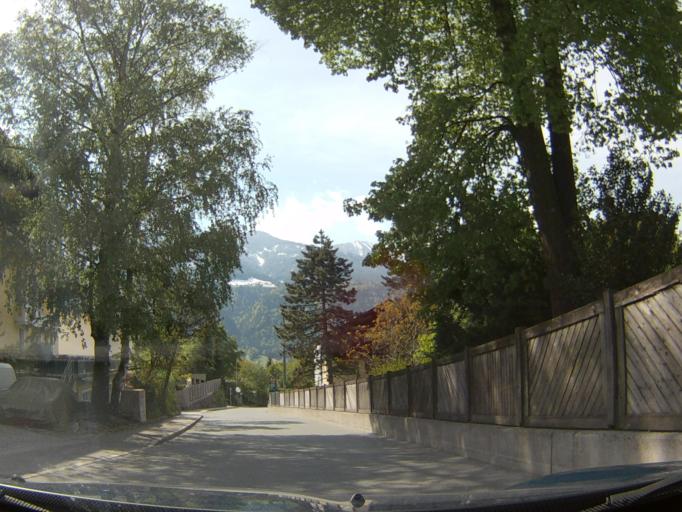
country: AT
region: Tyrol
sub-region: Politischer Bezirk Schwaz
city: Jenbach
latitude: 47.3948
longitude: 11.7711
